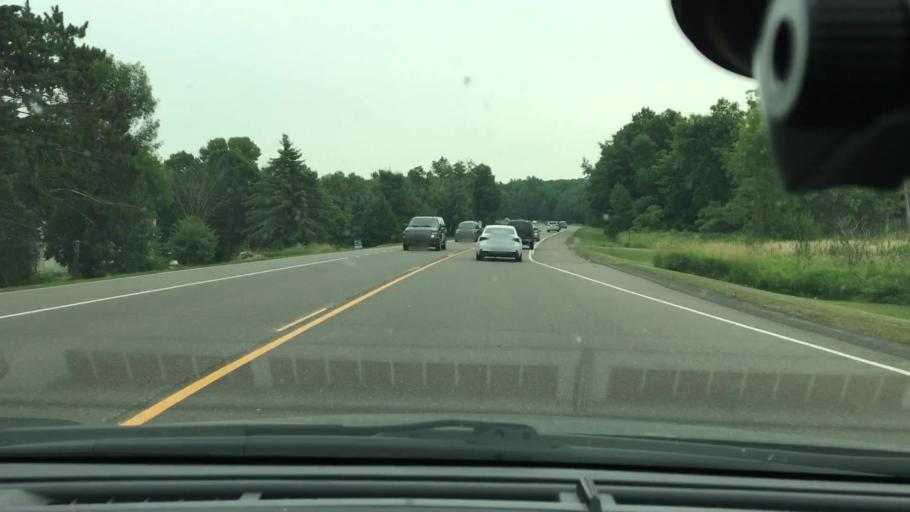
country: US
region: Minnesota
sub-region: Mille Lacs County
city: Vineland
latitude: 46.1340
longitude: -93.6913
